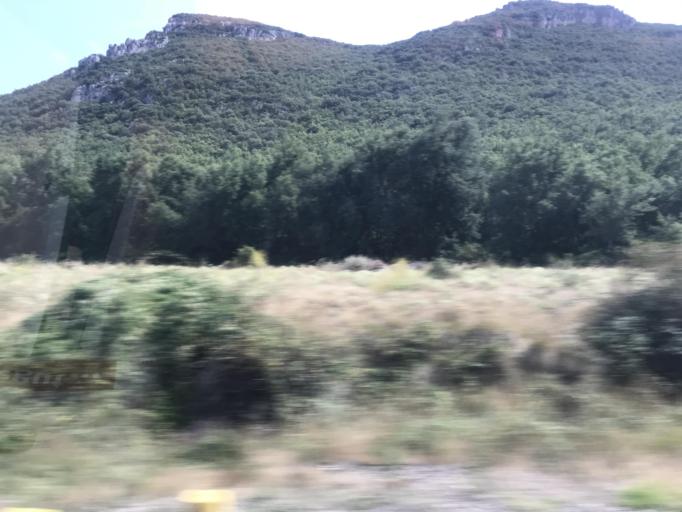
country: ES
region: Castille and Leon
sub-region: Provincia de Burgos
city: Bugedo
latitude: 42.6497
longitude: -3.0100
